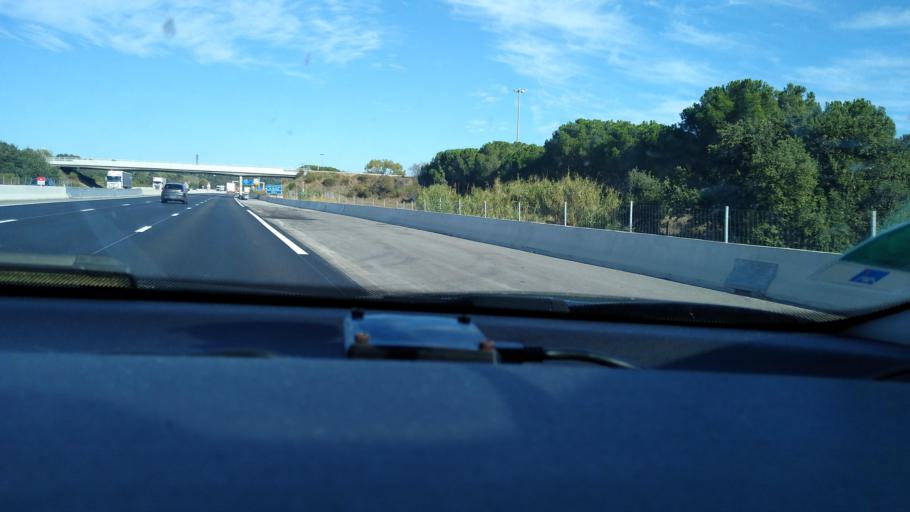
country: FR
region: Languedoc-Roussillon
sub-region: Departement des Pyrenees-Orientales
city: el Volo
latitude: 42.5193
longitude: 2.8191
